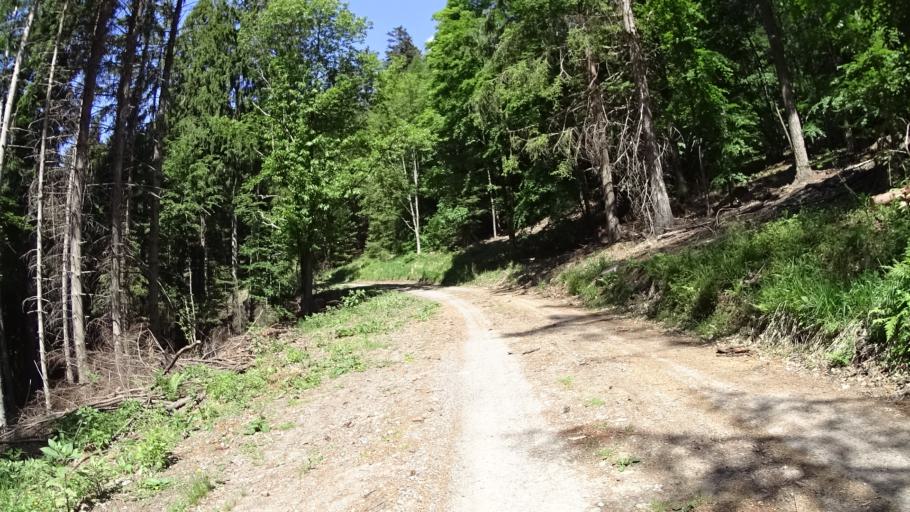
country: DE
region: Baden-Wuerttemberg
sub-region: Karlsruhe Region
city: Schonau
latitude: 49.4228
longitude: 8.7869
